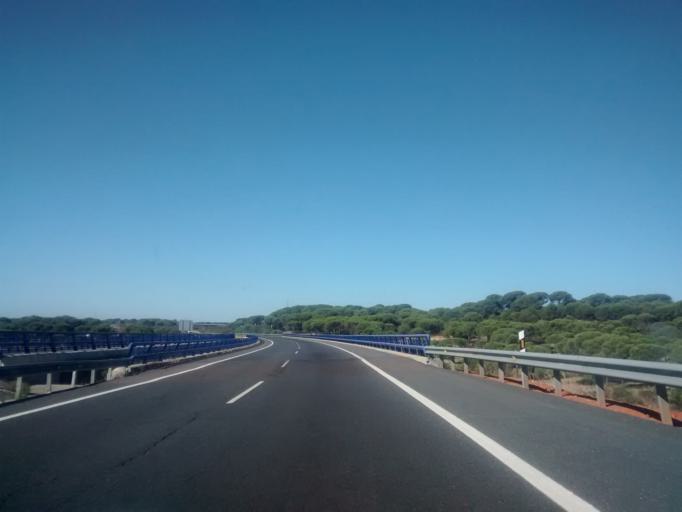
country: ES
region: Andalusia
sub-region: Provincia de Huelva
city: Cartaya
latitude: 37.3277
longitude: -7.1724
